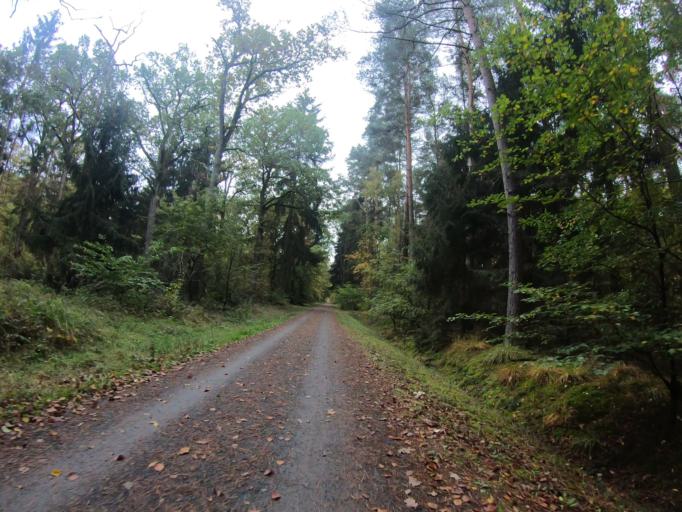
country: DE
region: Lower Saxony
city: Gifhorn
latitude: 52.4562
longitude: 10.5633
